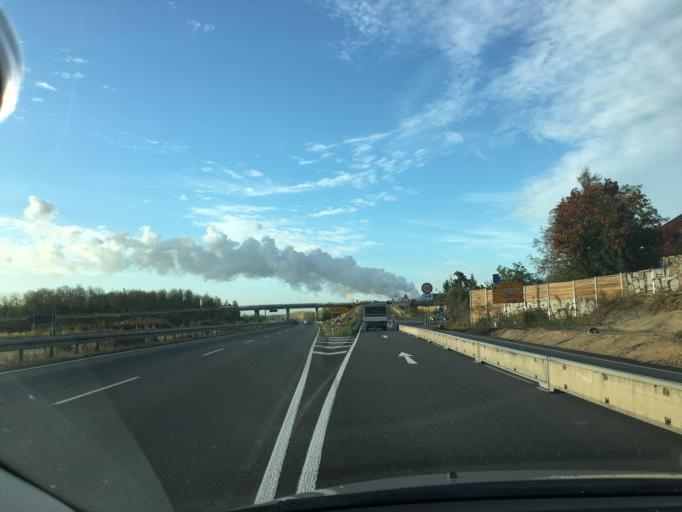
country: DE
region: Saxony
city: Bohlen
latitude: 51.2288
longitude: 12.3881
